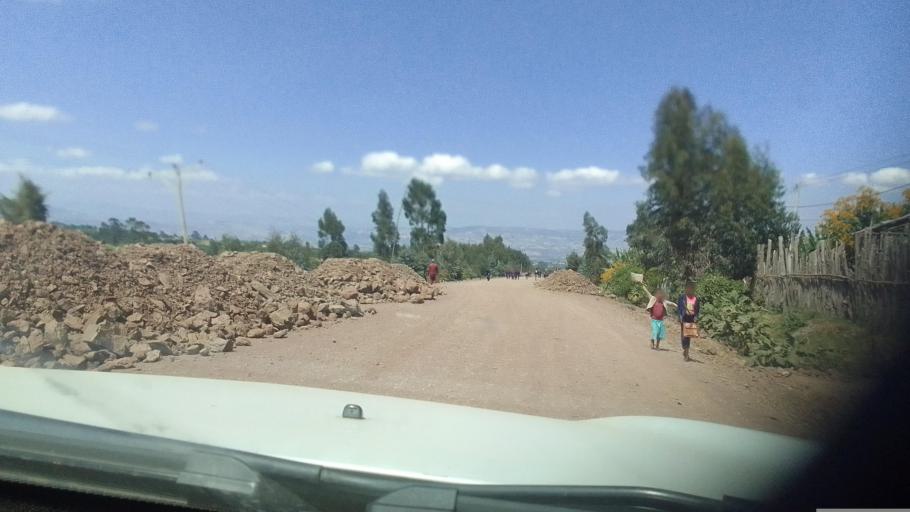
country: ET
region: Oromiya
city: Hagere Hiywet
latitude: 8.8581
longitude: 37.8916
